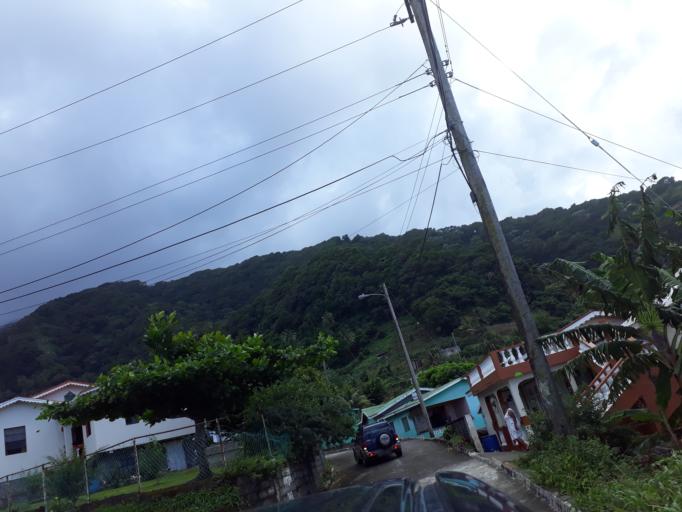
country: VC
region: Charlotte
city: Georgetown
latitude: 13.3801
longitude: -61.1709
